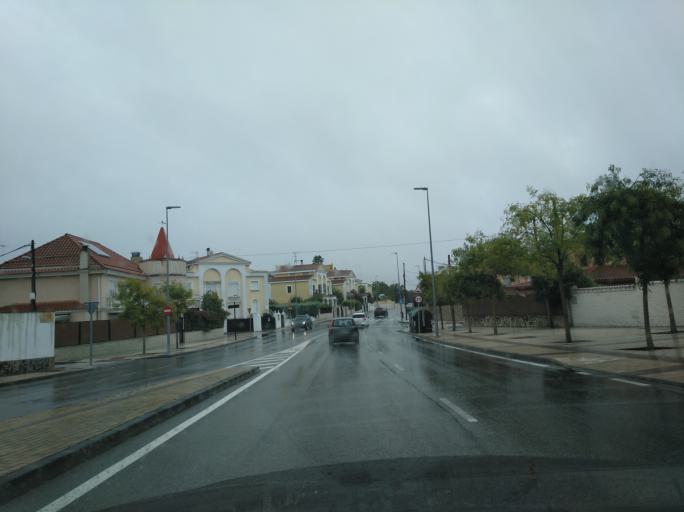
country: ES
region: Extremadura
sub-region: Provincia de Badajoz
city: Badajoz
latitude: 38.8880
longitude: -6.9916
